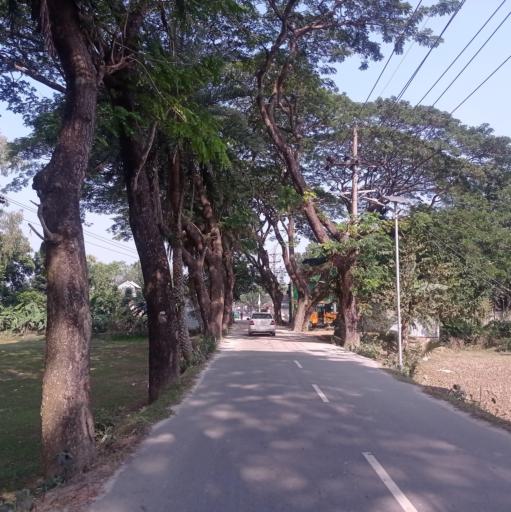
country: BD
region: Dhaka
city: Narsingdi
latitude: 24.0655
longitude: 90.6908
